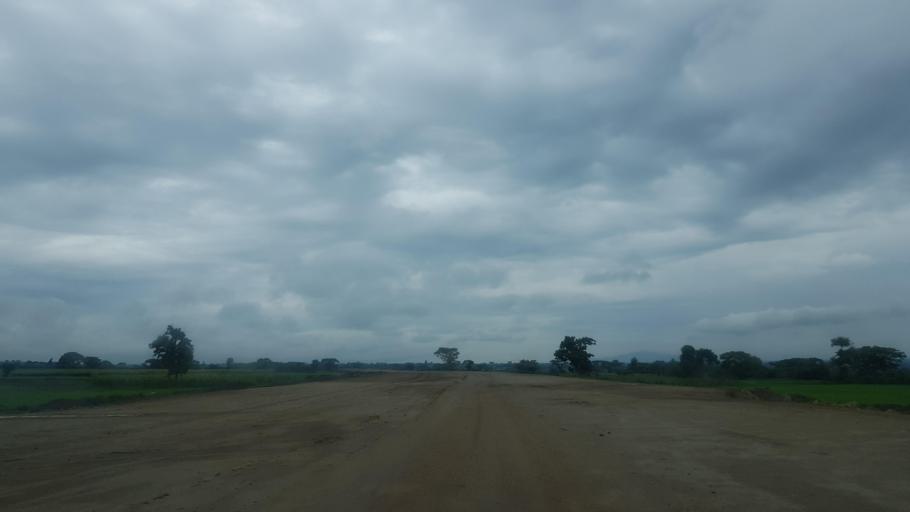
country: ET
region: Oromiya
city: Shashemene
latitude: 7.3865
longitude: 38.6505
